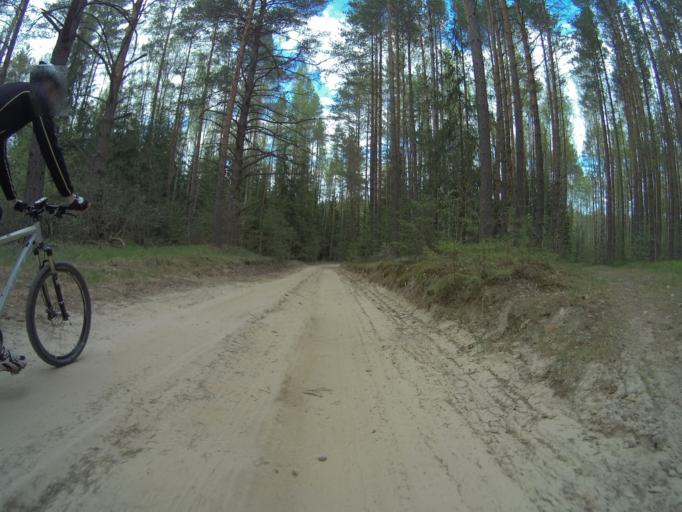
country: RU
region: Vladimir
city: Orgtrud
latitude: 56.1098
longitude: 40.6492
